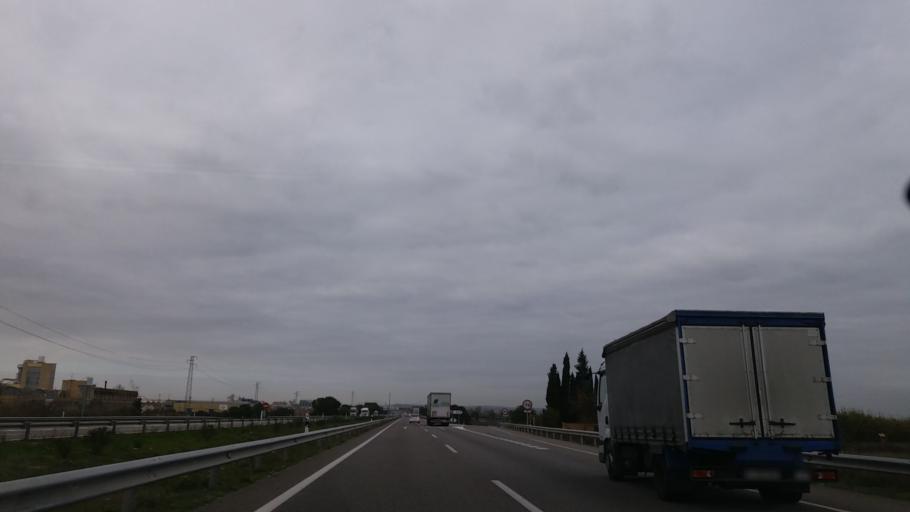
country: ES
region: Aragon
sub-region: Provincia de Zaragoza
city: Puebla de Alfinden
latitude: 41.6565
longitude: -0.7762
